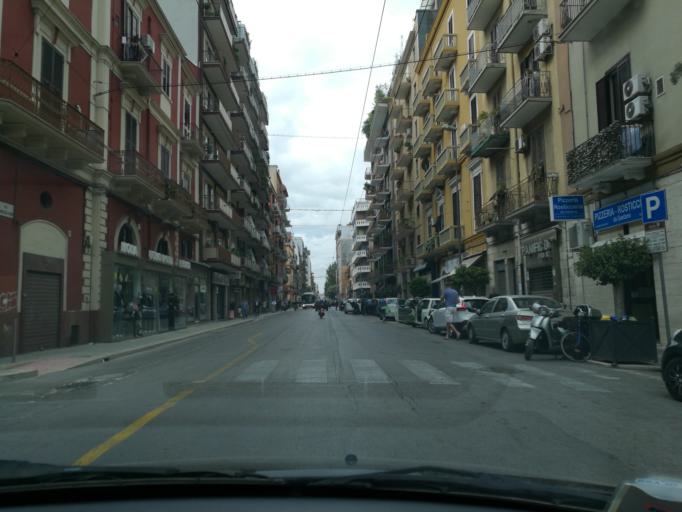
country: IT
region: Apulia
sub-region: Provincia di Bari
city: Bari
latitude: 41.1251
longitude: 16.8598
